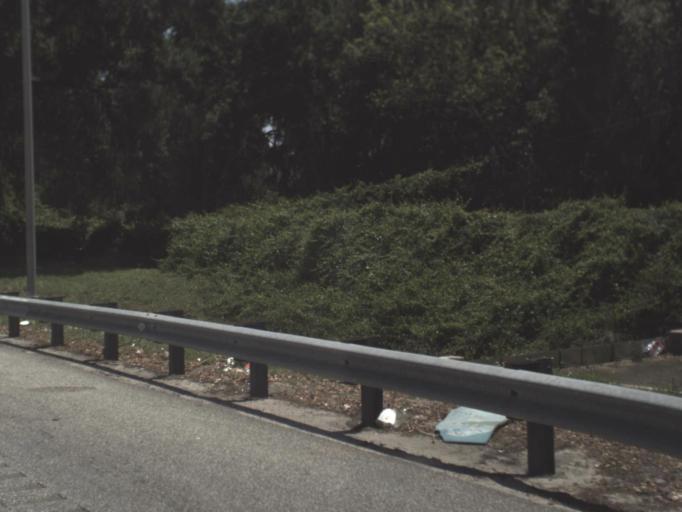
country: US
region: Florida
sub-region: Clay County
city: Orange Park
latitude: 30.1863
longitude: -81.6410
